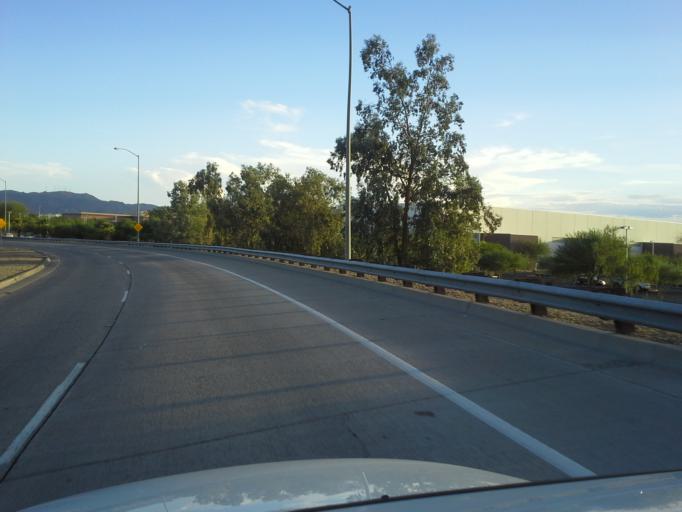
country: US
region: Arizona
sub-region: Maricopa County
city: Phoenix
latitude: 33.4394
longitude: -112.0384
